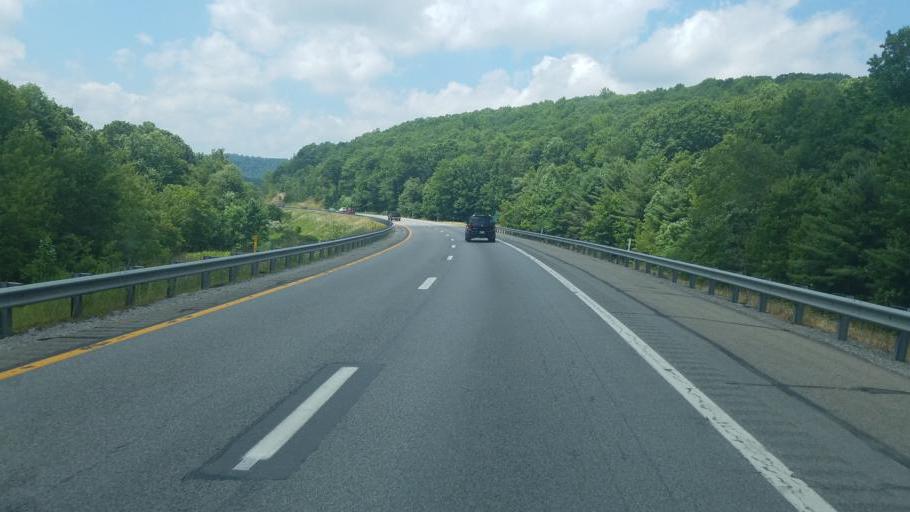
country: US
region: West Virginia
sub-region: Raleigh County
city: Shady Spring
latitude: 37.6949
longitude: -81.1305
